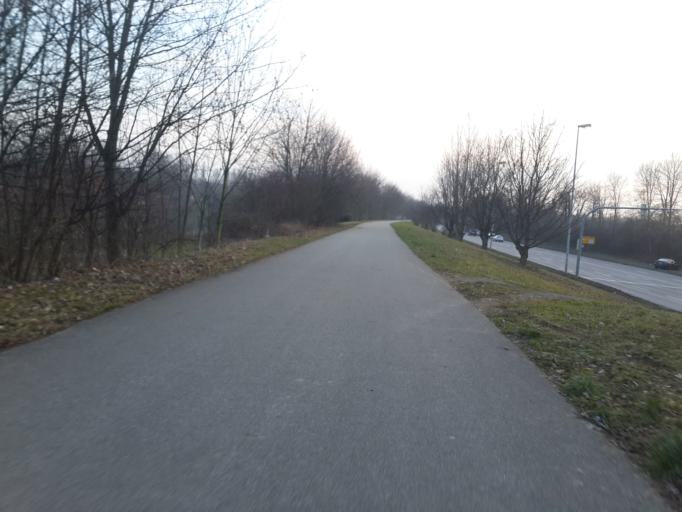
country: DE
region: Baden-Wuerttemberg
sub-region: Regierungsbezirk Stuttgart
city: Heilbronn
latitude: 49.1314
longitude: 9.1982
